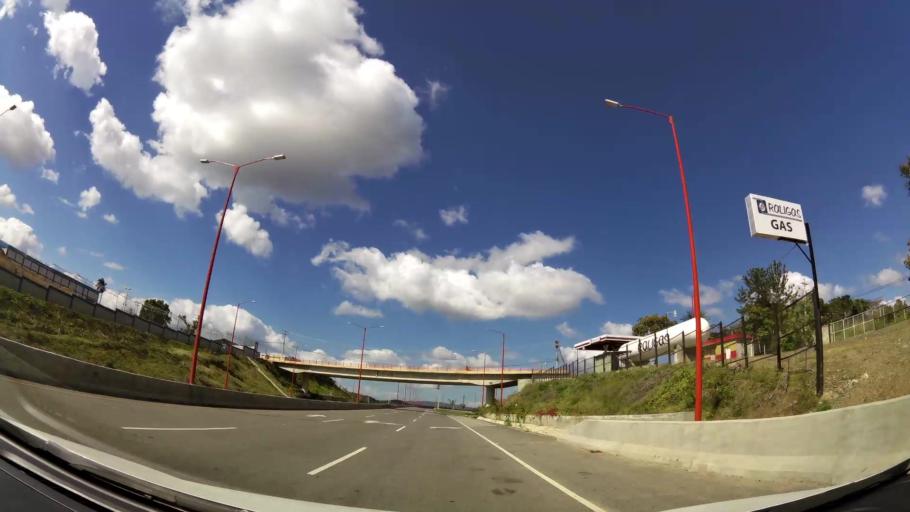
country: DO
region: Santo Domingo
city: Santo Domingo Oeste
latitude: 18.5595
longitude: -70.0699
